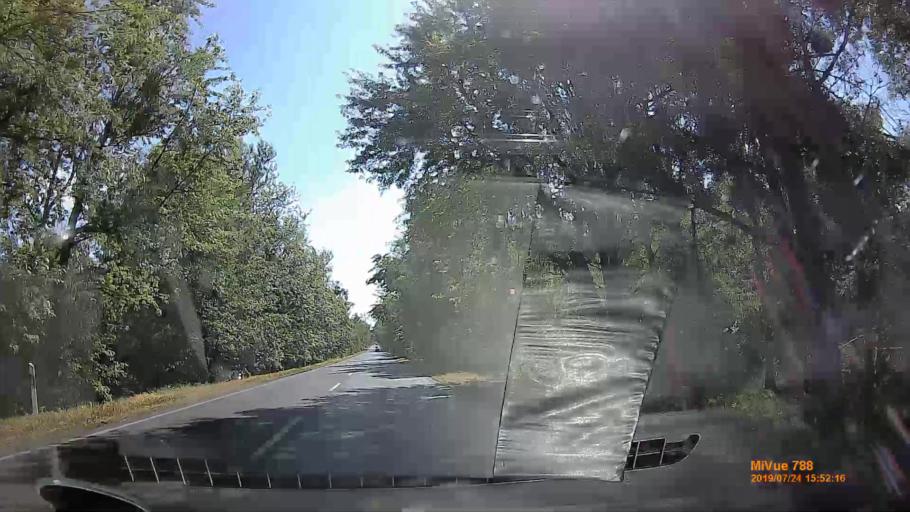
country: HU
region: Szabolcs-Szatmar-Bereg
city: Vaja
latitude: 48.0317
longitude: 22.1688
